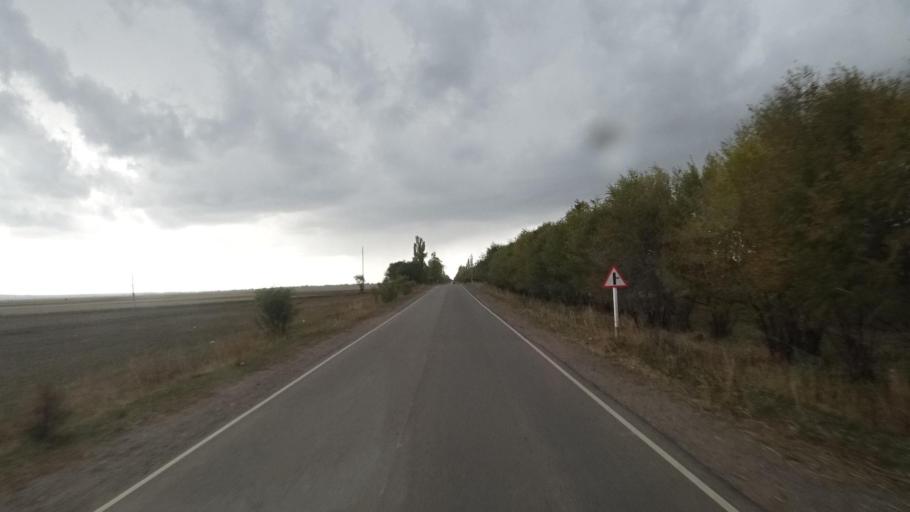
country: KG
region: Ysyk-Koel
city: Tyup
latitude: 42.7461
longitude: 78.4272
